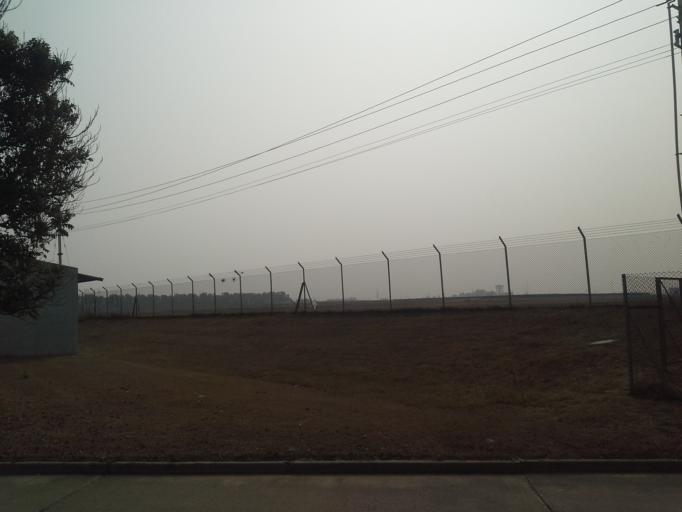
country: IN
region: Telangana
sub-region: Medak
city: Patancheru
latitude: 17.5098
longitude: 78.2756
